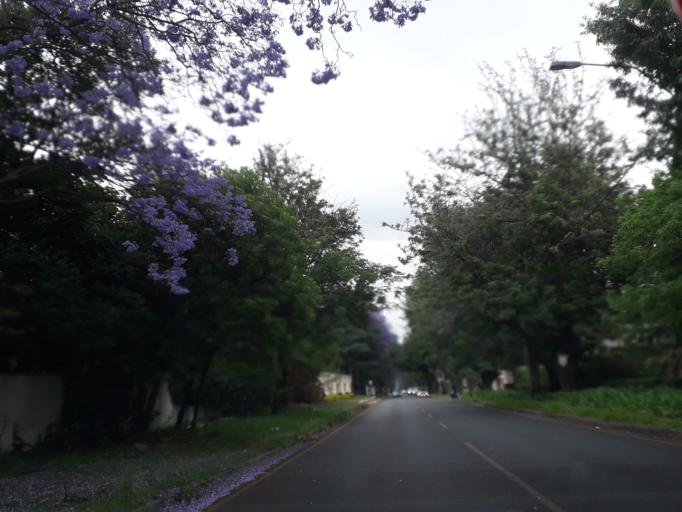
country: ZA
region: Gauteng
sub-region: City of Johannesburg Metropolitan Municipality
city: Johannesburg
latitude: -26.1689
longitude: 28.0617
